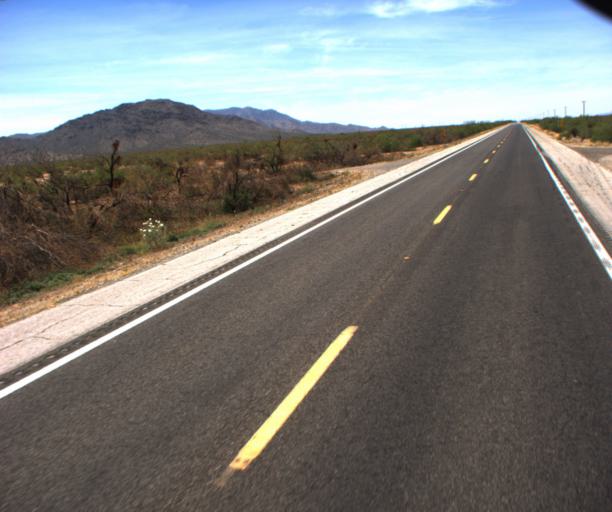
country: US
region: Arizona
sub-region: La Paz County
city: Salome
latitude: 33.9248
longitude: -113.2352
